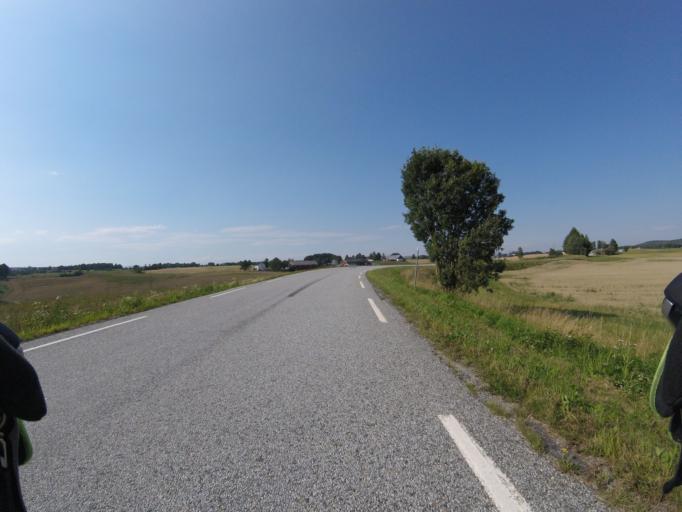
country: NO
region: Akershus
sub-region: Ullensaker
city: Klofta
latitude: 60.0906
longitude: 11.1611
